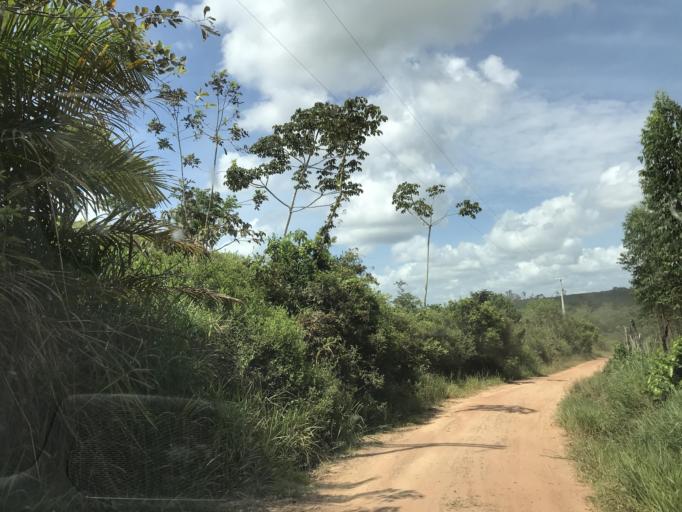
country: BR
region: Bahia
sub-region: Entre Rios
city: Entre Rios
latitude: -12.2184
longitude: -38.0764
